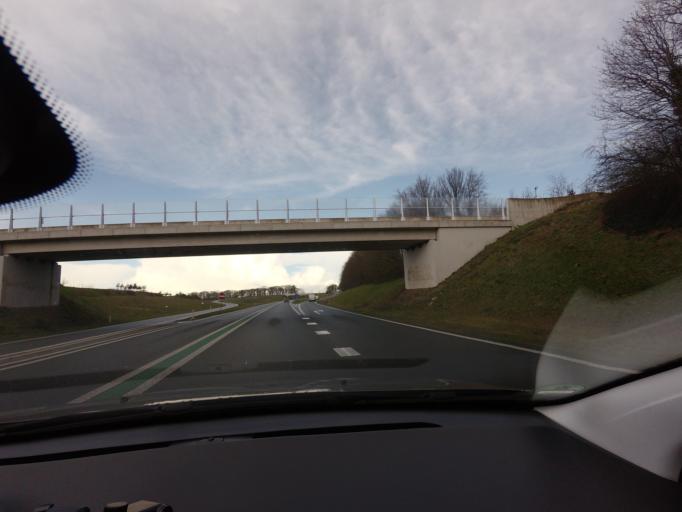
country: NL
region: Drenthe
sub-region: Gemeente Borger-Odoorn
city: Borger
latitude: 52.9204
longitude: 6.7870
